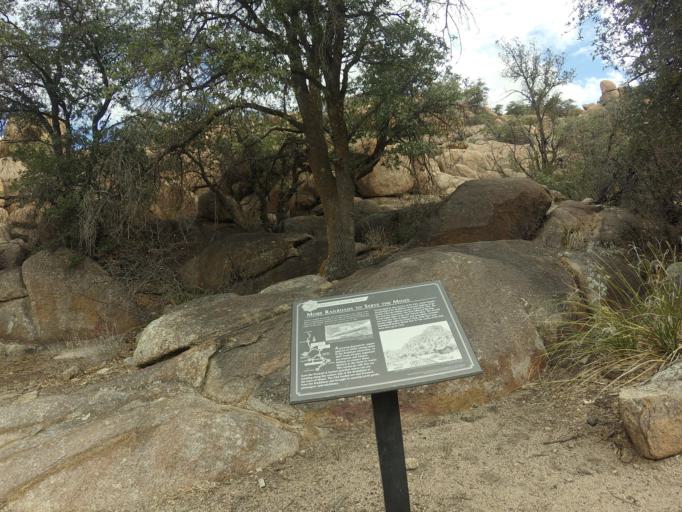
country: US
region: Arizona
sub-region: Yavapai County
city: Prescott Valley
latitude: 34.6067
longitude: -112.4043
